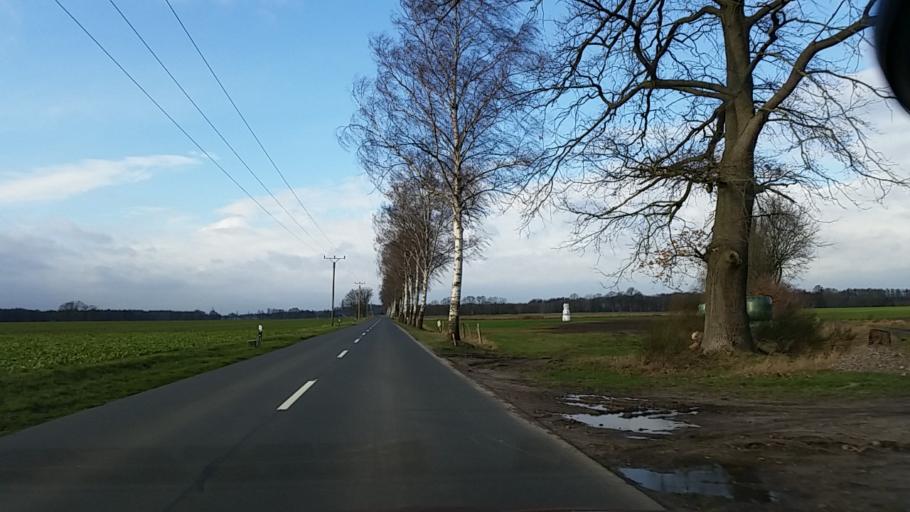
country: DE
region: Lower Saxony
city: Wrestedt
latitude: 52.9063
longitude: 10.5614
